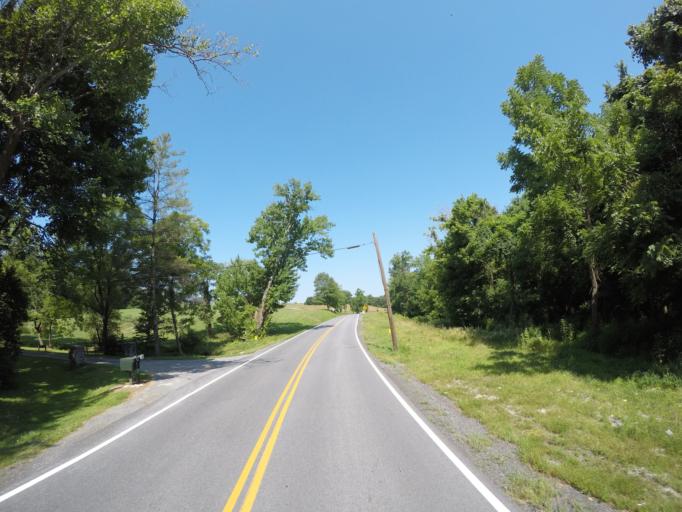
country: US
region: Maryland
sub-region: Frederick County
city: Bartonsville
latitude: 39.3628
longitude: -77.3291
